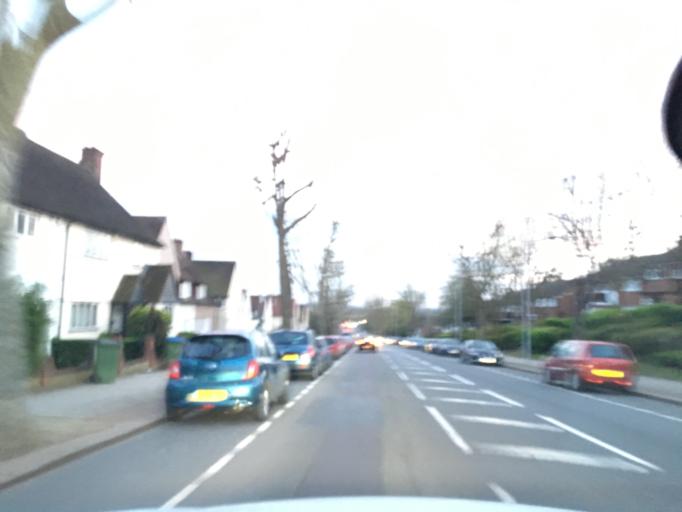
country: GB
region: England
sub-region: Greater London
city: Woolwich
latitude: 51.4658
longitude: 0.0519
